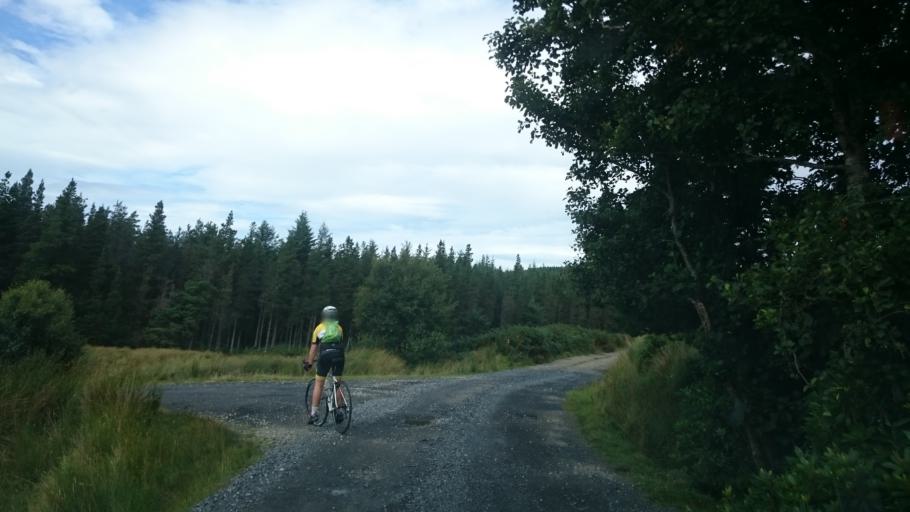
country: IE
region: Connaught
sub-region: Maigh Eo
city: Westport
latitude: 53.9896
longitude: -9.5721
